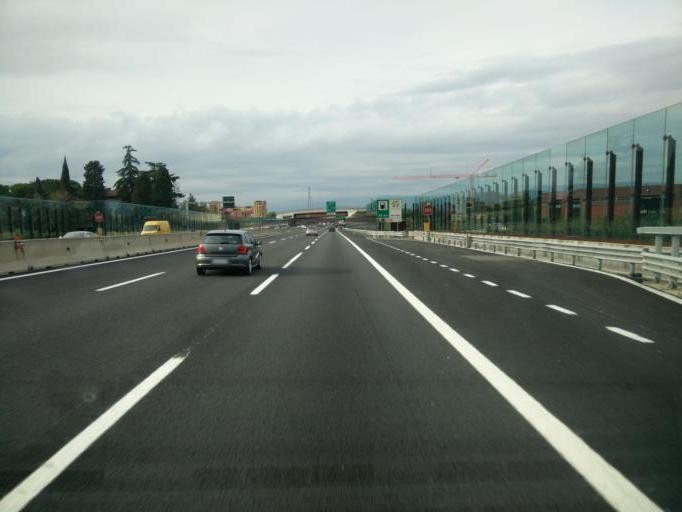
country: IT
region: Tuscany
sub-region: Province of Florence
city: Mantignano-Ugnano
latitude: 43.7671
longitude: 11.1666
